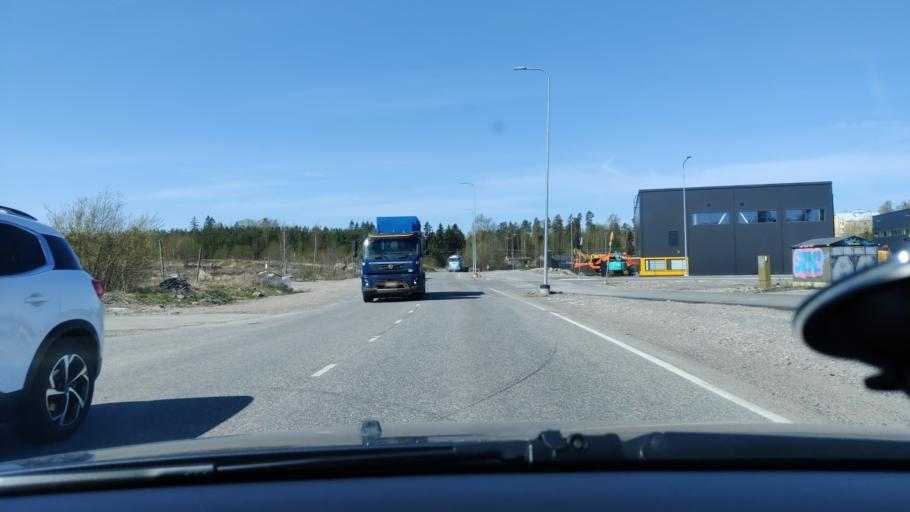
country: FI
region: Uusimaa
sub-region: Helsinki
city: Kerava
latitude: 60.3749
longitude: 25.1007
